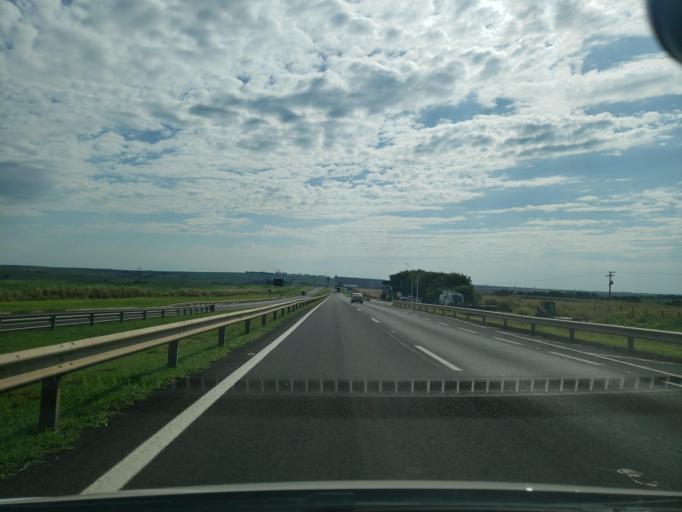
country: BR
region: Sao Paulo
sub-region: Lins
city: Lins
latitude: -21.6597
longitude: -49.7985
